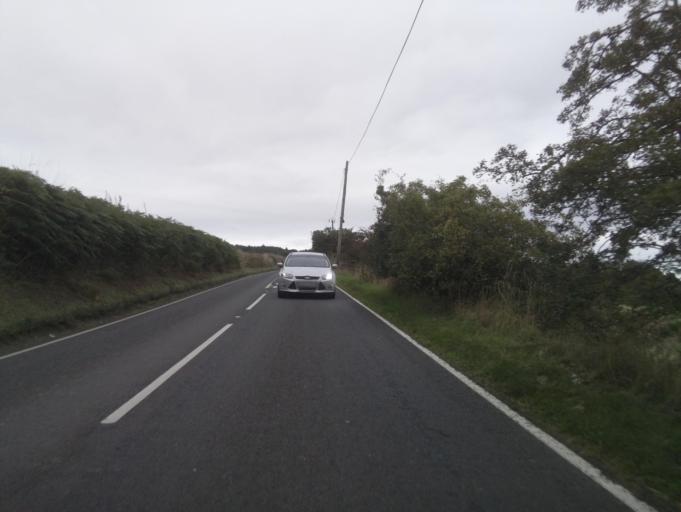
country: GB
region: Scotland
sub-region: Fife
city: Kinglassie
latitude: 56.1978
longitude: -3.2571
